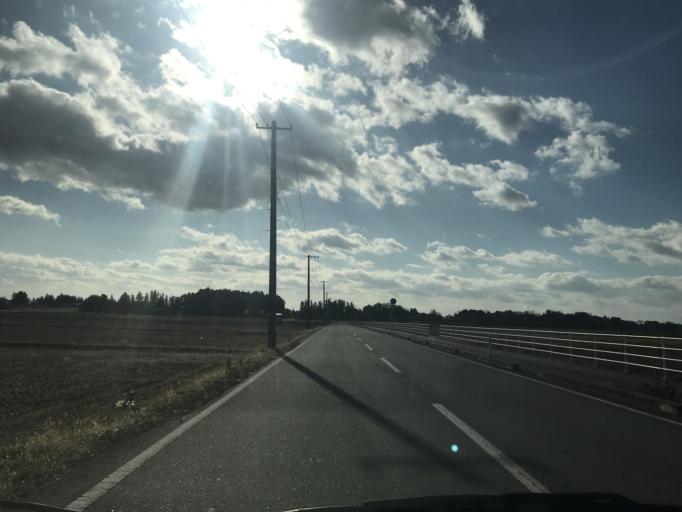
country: JP
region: Iwate
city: Ichinoseki
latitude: 38.7684
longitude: 141.0593
